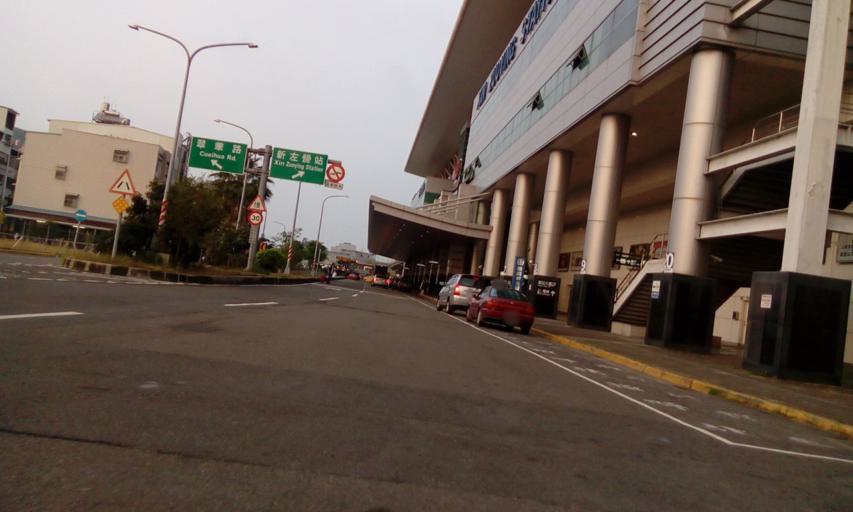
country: TW
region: Kaohsiung
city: Kaohsiung
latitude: 22.6871
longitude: 120.3061
